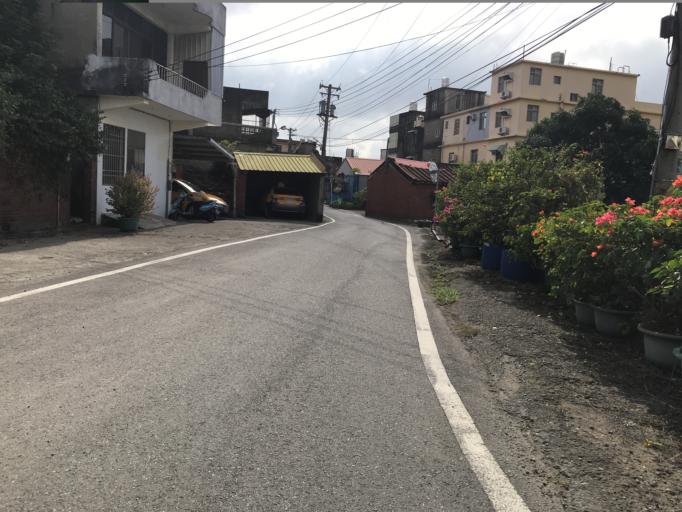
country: TW
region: Taiwan
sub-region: Hsinchu
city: Zhubei
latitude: 24.8130
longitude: 120.9974
